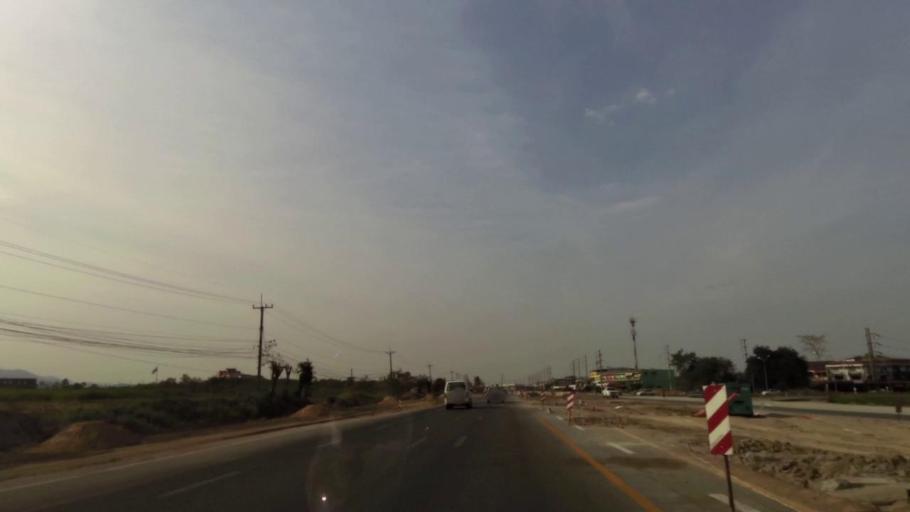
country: TH
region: Chon Buri
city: Ban Bueng
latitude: 13.2840
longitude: 101.1790
